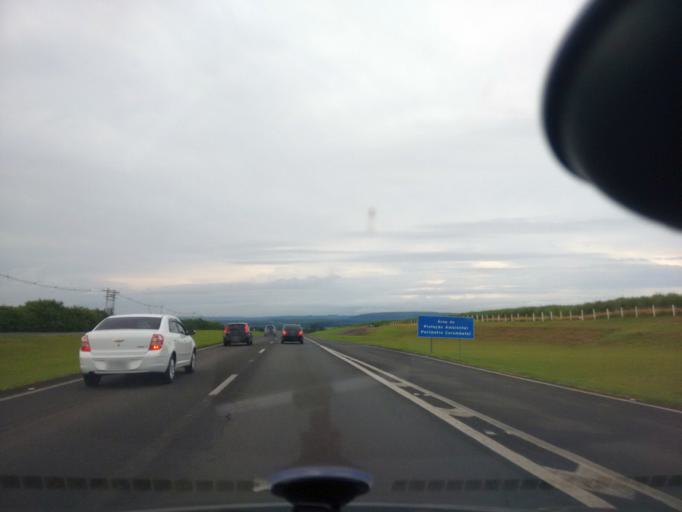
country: BR
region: Sao Paulo
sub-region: Itirapina
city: Itirapina
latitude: -22.1892
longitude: -47.7781
